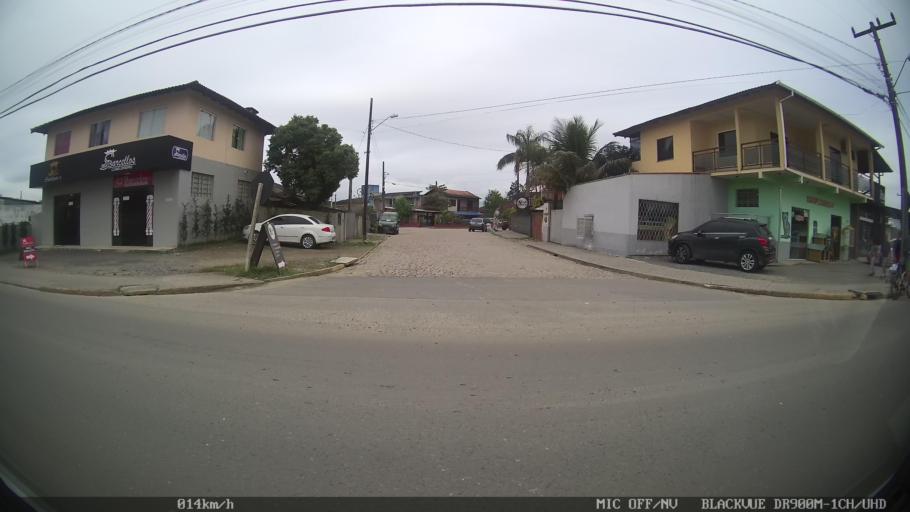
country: BR
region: Santa Catarina
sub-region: Joinville
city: Joinville
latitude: -26.3286
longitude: -48.9081
